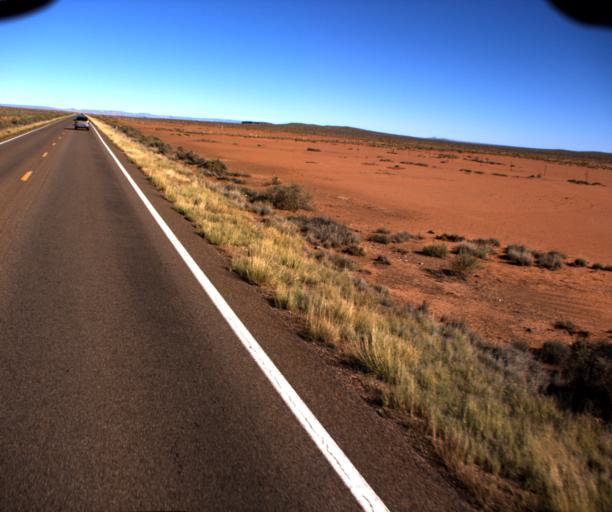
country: US
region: Arizona
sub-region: Navajo County
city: Holbrook
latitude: 34.8061
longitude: -110.1368
